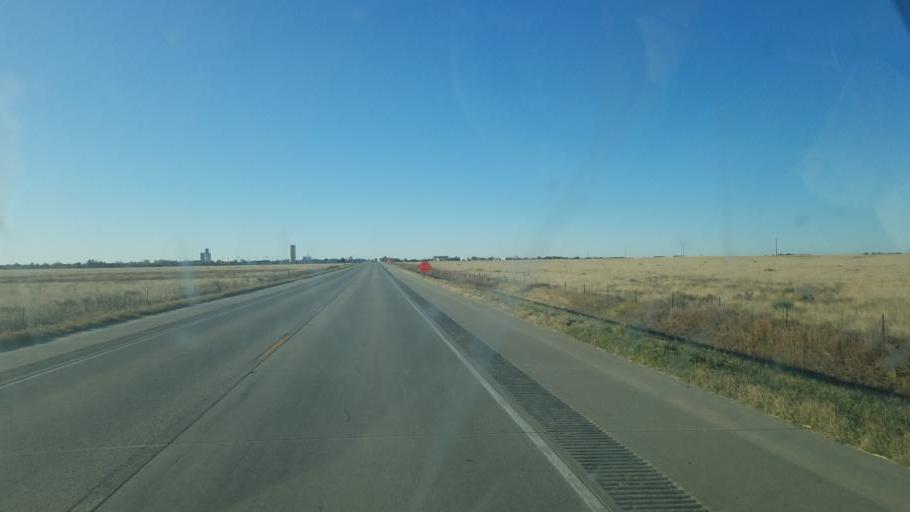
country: US
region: Colorado
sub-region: Kiowa County
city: Eads
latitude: 38.4983
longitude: -102.7857
